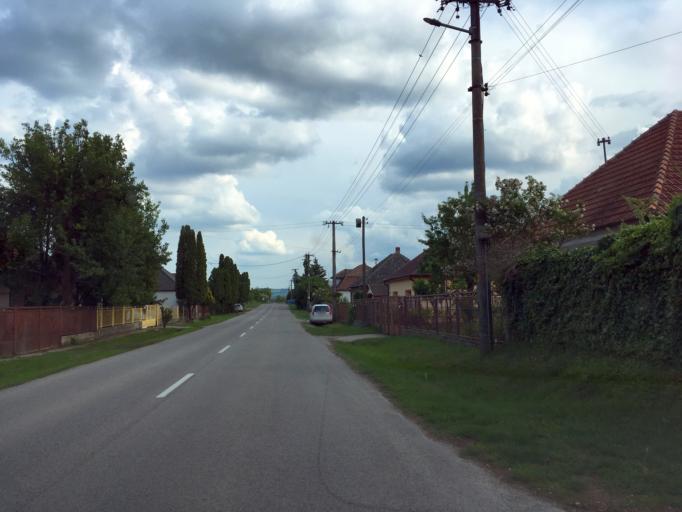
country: HU
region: Komarom-Esztergom
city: Dunaalmas
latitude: 47.7762
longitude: 18.2990
